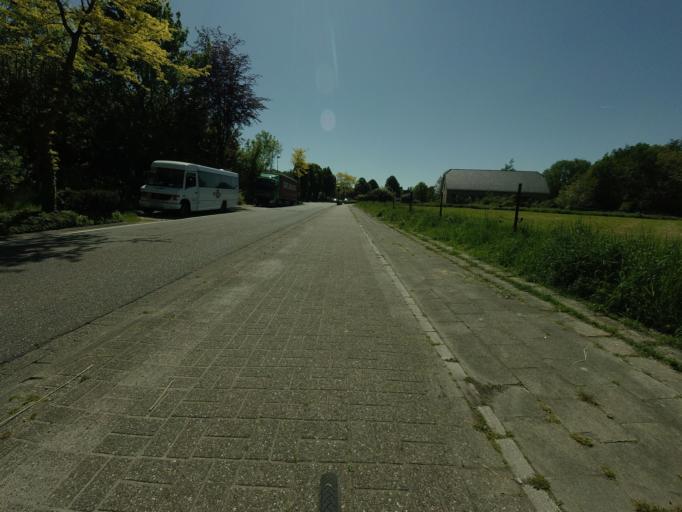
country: BE
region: Flanders
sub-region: Provincie Antwerpen
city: Mortsel
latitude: 51.1759
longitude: 4.4684
